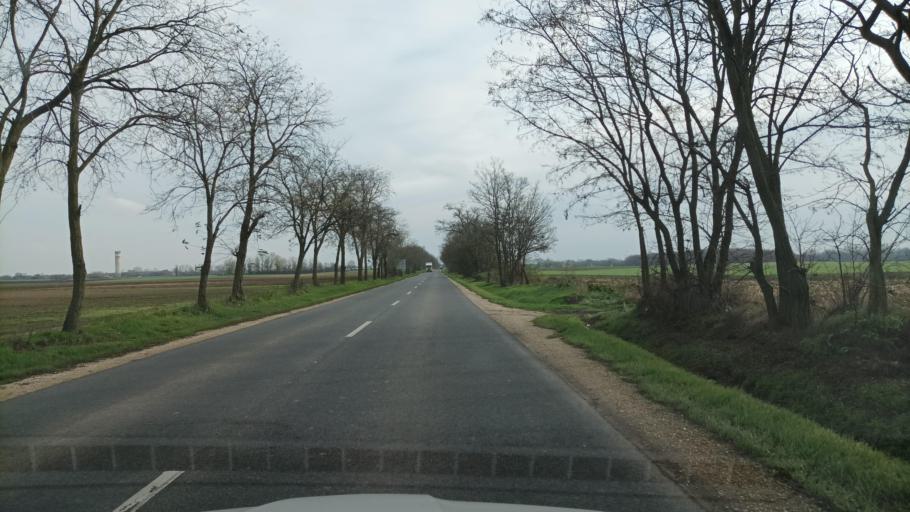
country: HU
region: Pest
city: Ocsa
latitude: 47.3144
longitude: 19.2045
